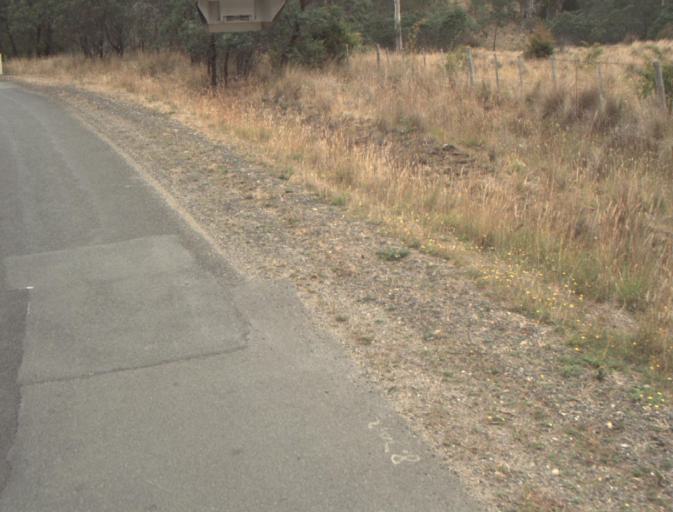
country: AU
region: Tasmania
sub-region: Northern Midlands
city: Evandale
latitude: -41.5071
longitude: 147.3804
